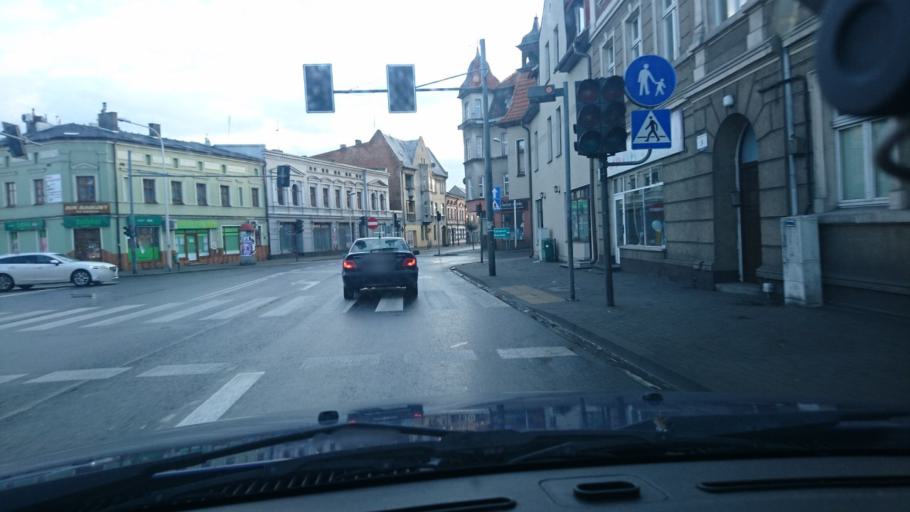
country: PL
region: Greater Poland Voivodeship
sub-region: Powiat kepinski
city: Kepno
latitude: 51.2852
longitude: 17.9930
